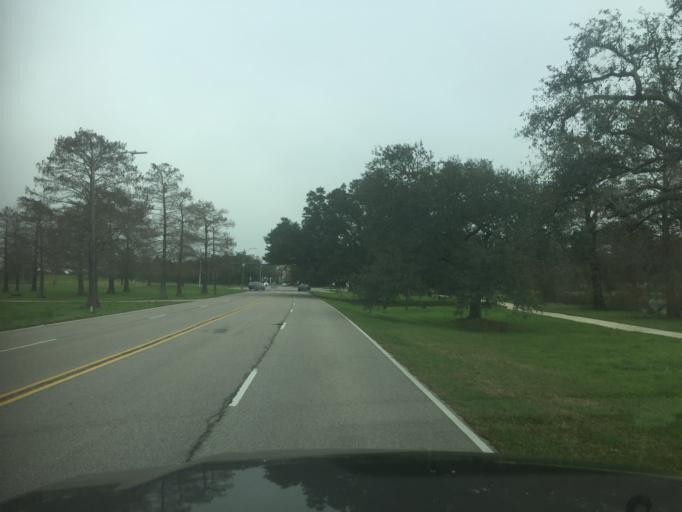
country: US
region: Louisiana
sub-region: Jefferson Parish
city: Metairie
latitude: 30.0174
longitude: -90.0968
